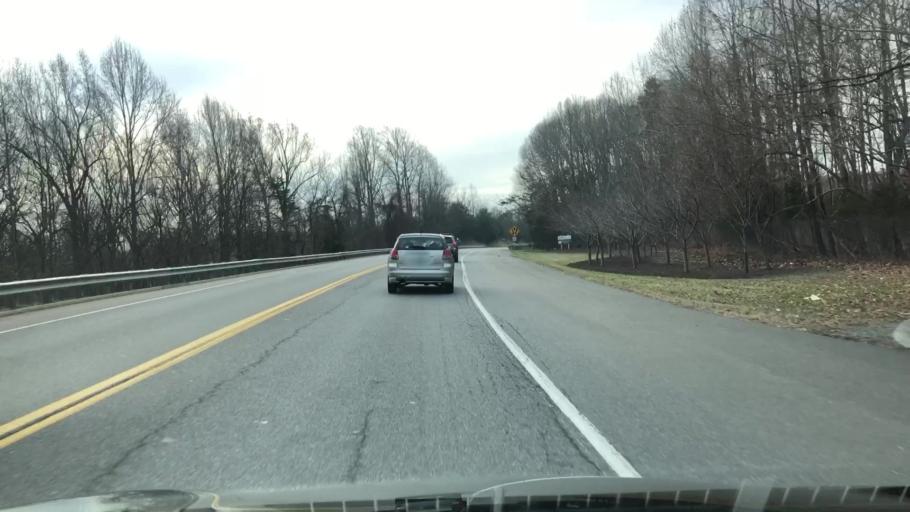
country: US
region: Virginia
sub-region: City of Lynchburg
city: West Lynchburg
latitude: 37.4225
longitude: -79.2317
